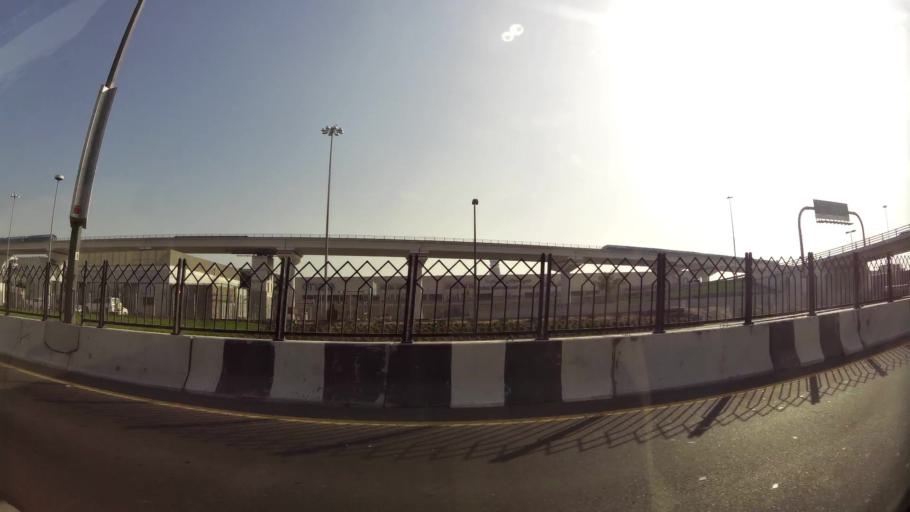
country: AE
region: Ash Shariqah
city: Sharjah
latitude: 25.2466
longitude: 55.3543
